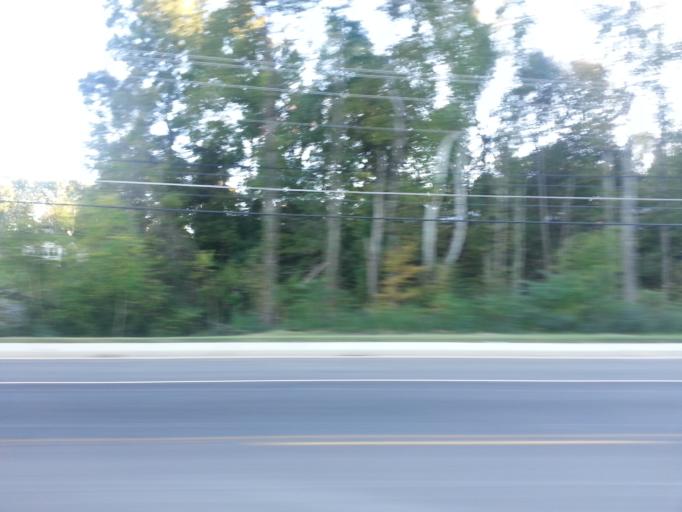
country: US
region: Tennessee
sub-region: Knox County
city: Knoxville
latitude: 35.9838
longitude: -84.0266
